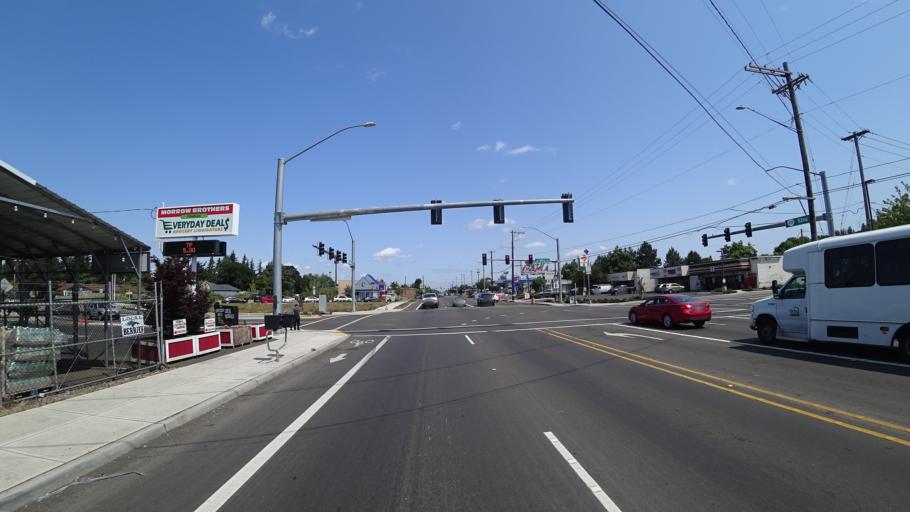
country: US
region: Oregon
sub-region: Multnomah County
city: Lents
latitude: 45.4512
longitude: -122.5792
